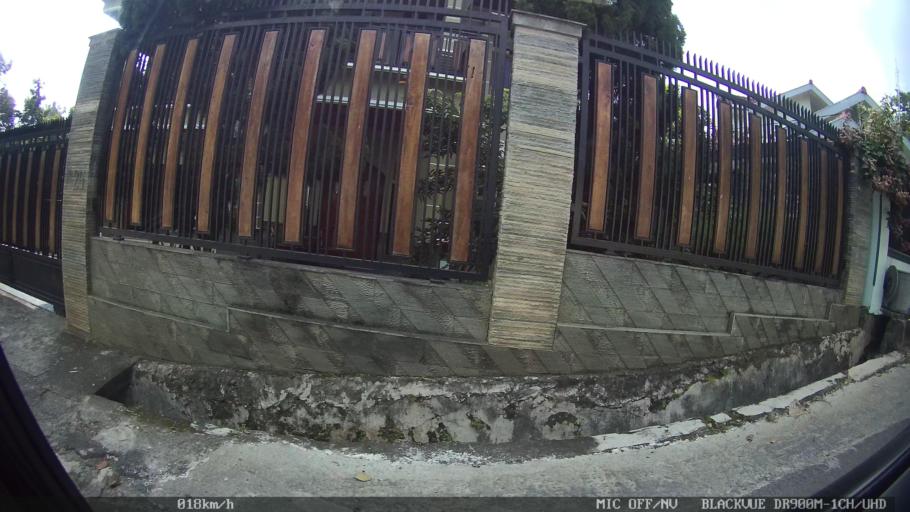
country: ID
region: Lampung
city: Bandarlampung
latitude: -5.4296
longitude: 105.2490
